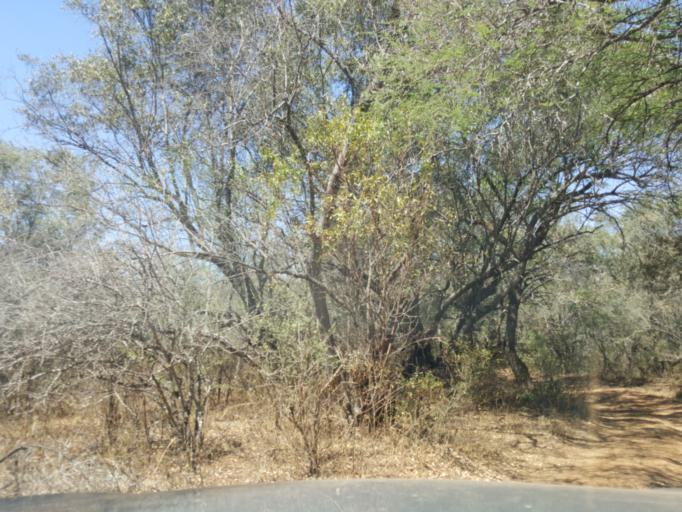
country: BW
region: South East
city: Lobatse
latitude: -25.1593
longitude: 25.6778
